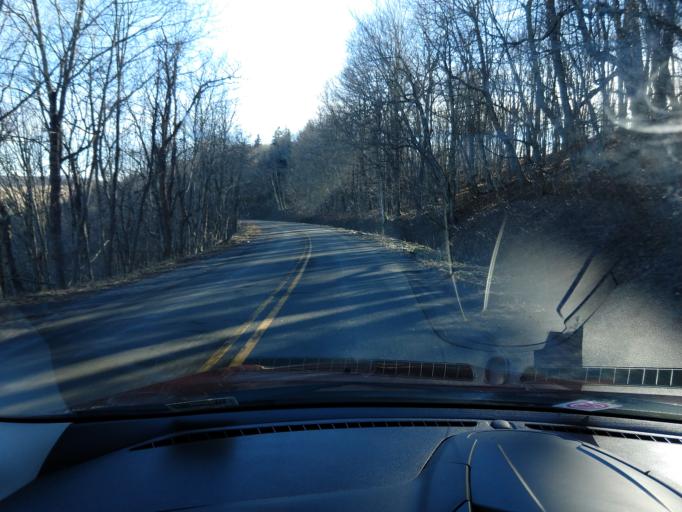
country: US
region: Virginia
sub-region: Highland County
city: Monterey
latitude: 38.4626
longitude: -79.6898
